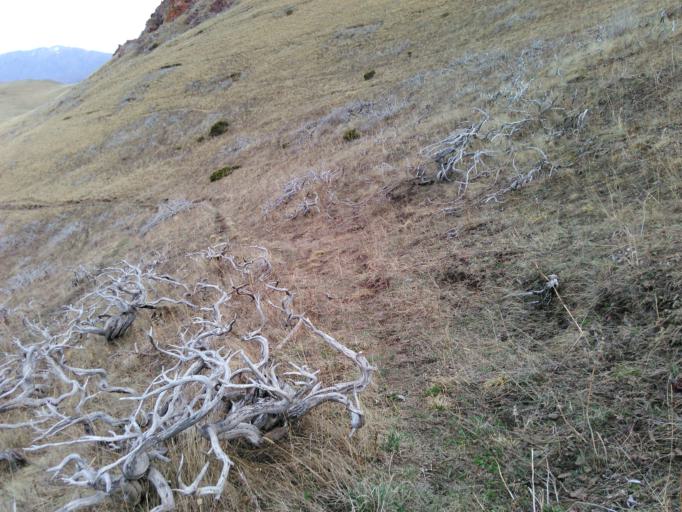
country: KG
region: Naryn
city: Kochkor
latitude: 42.4984
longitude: 75.7333
